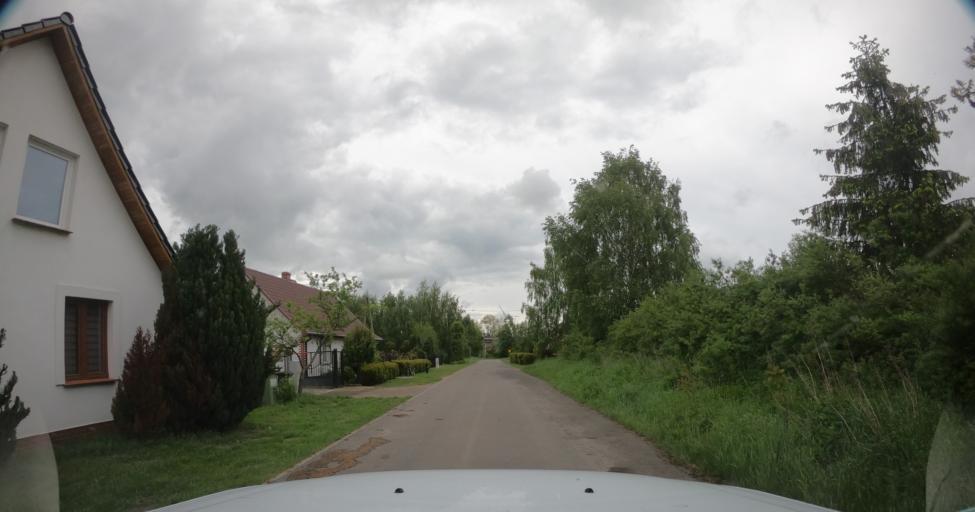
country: PL
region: West Pomeranian Voivodeship
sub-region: Powiat pyrzycki
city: Kozielice
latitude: 53.1064
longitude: 14.8133
